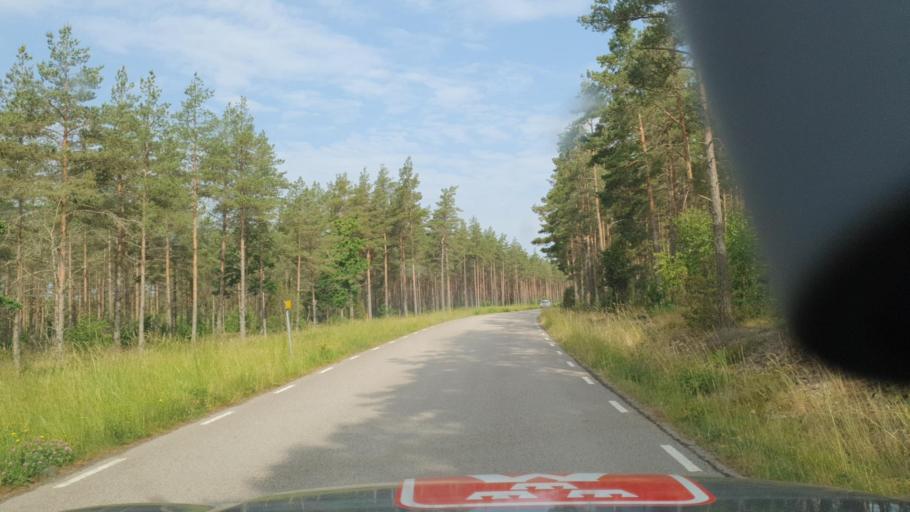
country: SE
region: Kalmar
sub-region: Kalmar Kommun
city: Ljungbyholm
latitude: 56.6098
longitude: 16.0667
